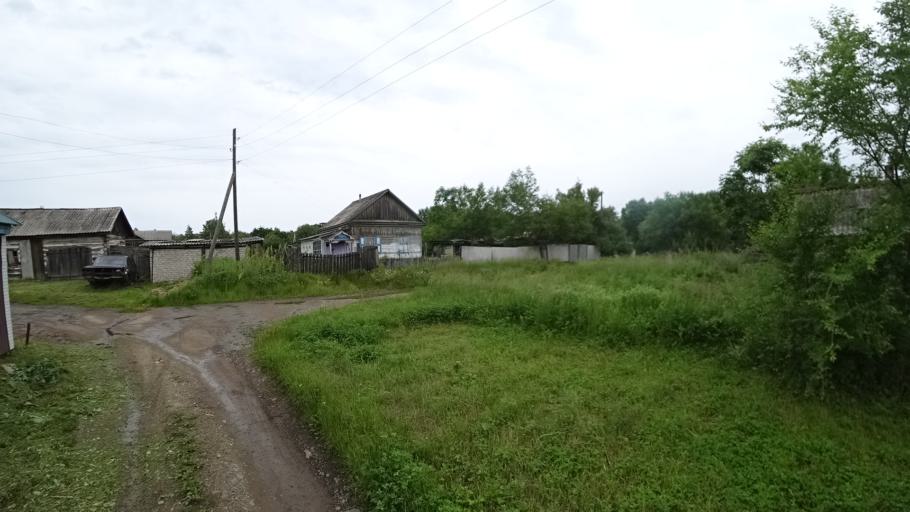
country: RU
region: Primorskiy
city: Novosysoyevka
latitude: 44.2084
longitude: 133.3380
